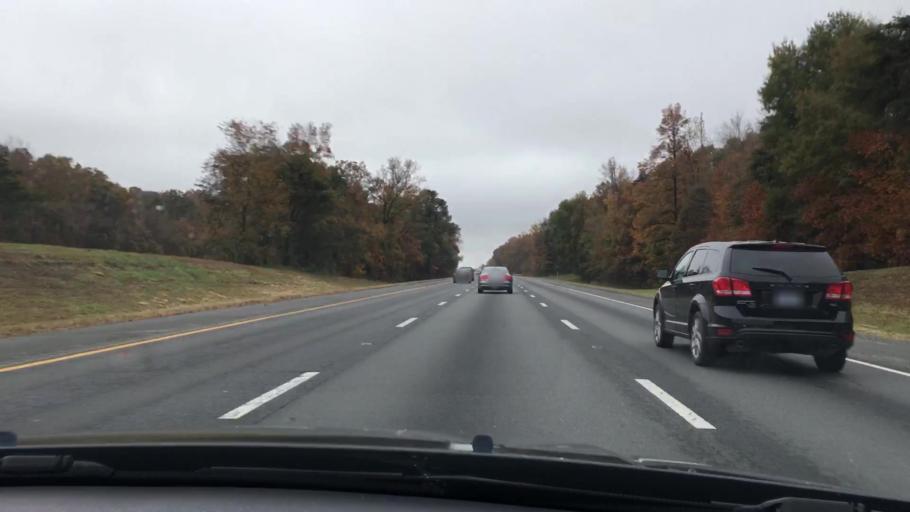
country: US
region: Virginia
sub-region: Spotsylvania County
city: Spotsylvania Courthouse
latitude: 38.1067
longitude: -77.5182
